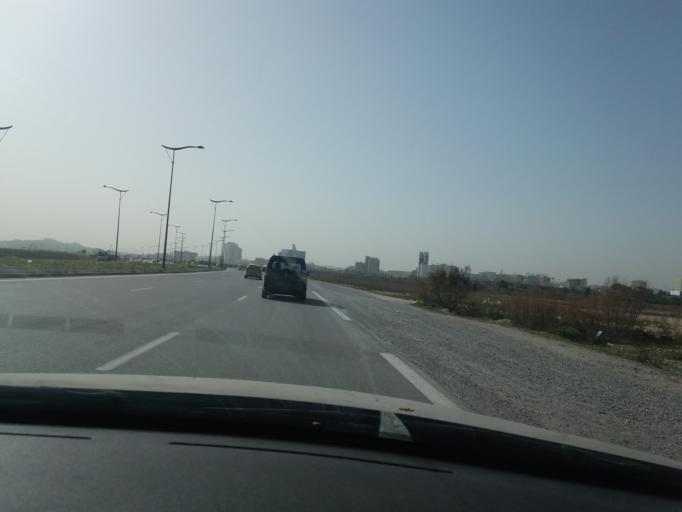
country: TN
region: Tunis
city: Tunis
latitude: 36.8178
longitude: 10.1967
